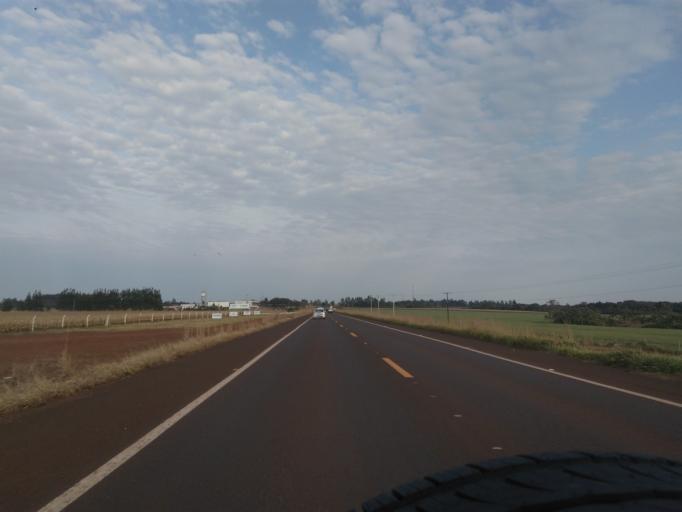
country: BR
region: Mato Grosso do Sul
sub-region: Ponta Pora
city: Ponta Pora
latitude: -22.6170
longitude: -55.6032
